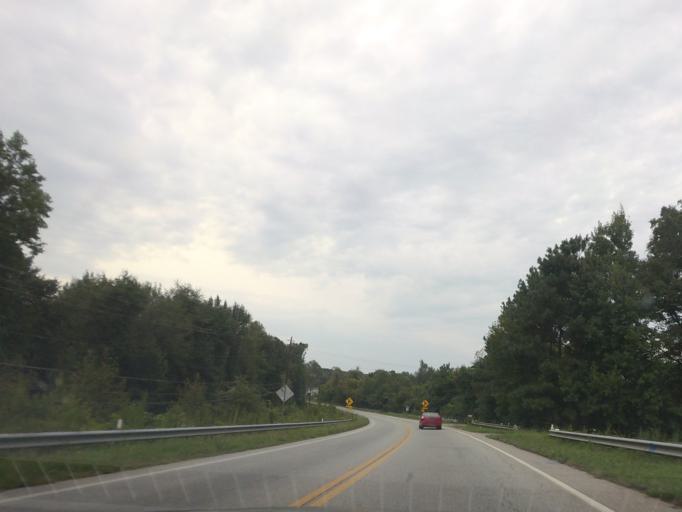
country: US
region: Georgia
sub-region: Bibb County
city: Macon
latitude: 32.8028
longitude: -83.5013
